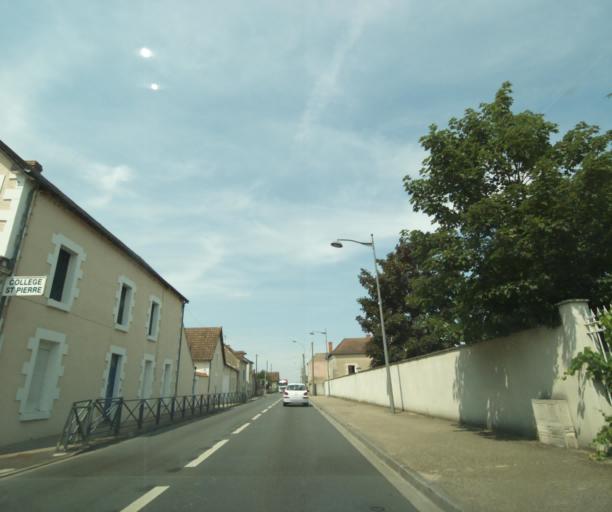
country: FR
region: Poitou-Charentes
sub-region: Departement de la Vienne
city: Dange-Saint-Romain
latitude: 46.9385
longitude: 0.6067
